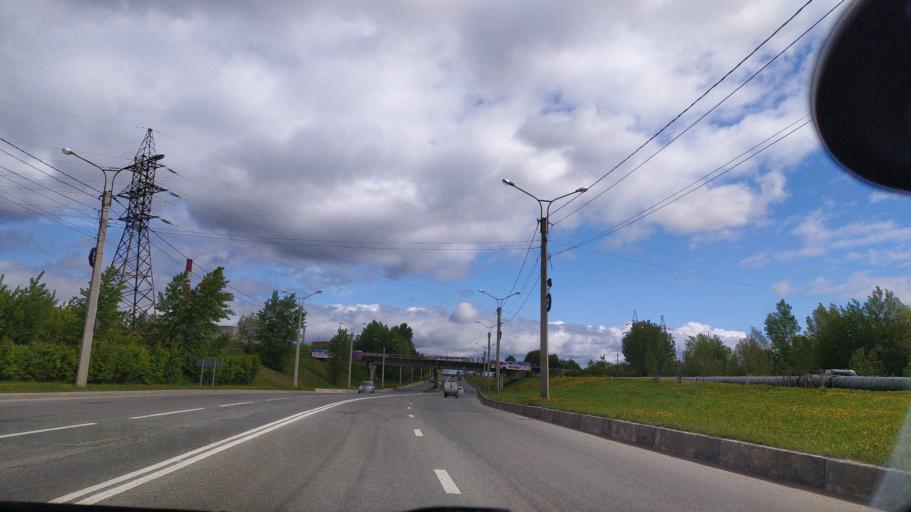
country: RU
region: Chuvashia
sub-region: Cheboksarskiy Rayon
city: Cheboksary
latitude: 56.1117
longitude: 47.2959
